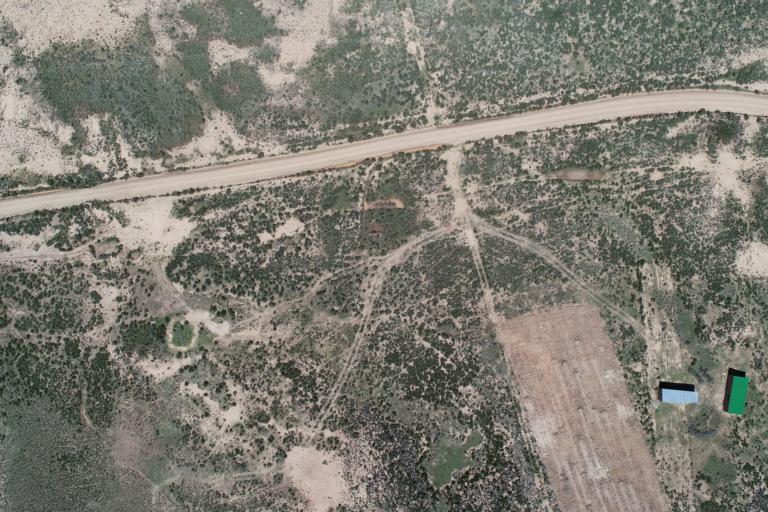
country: BO
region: La Paz
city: Patacamaya
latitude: -17.2920
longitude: -68.4872
